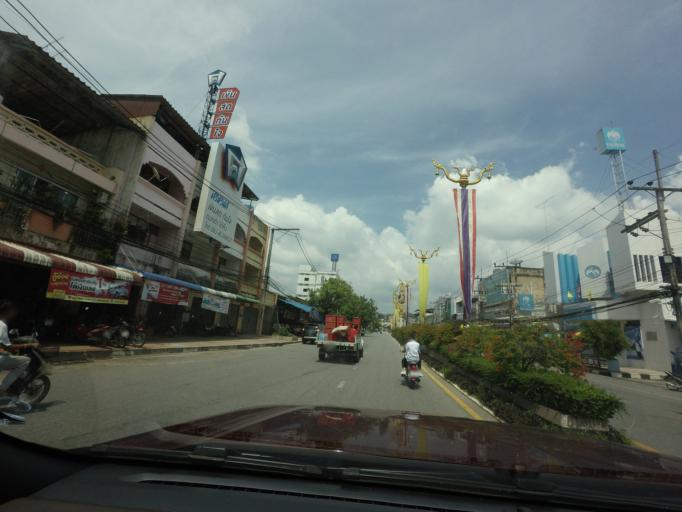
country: TH
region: Yala
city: Betong
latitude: 5.7769
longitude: 101.0733
